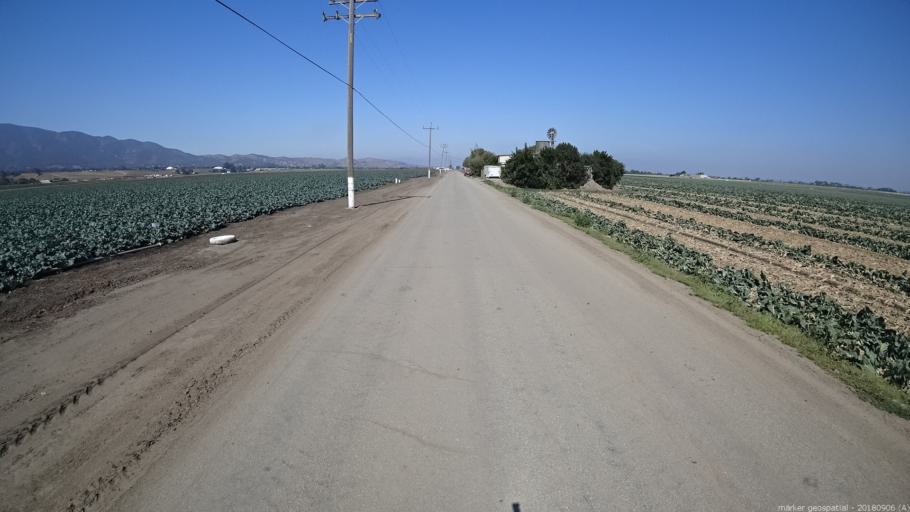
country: US
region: California
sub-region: Monterey County
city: Chualar
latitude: 36.5976
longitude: -121.6059
